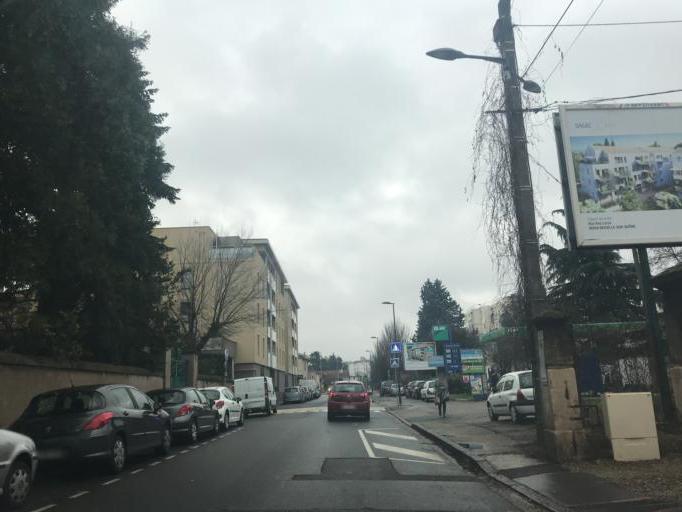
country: FR
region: Rhone-Alpes
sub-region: Departement du Rhone
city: Albigny-sur-Saone
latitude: 45.8730
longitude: 4.8393
